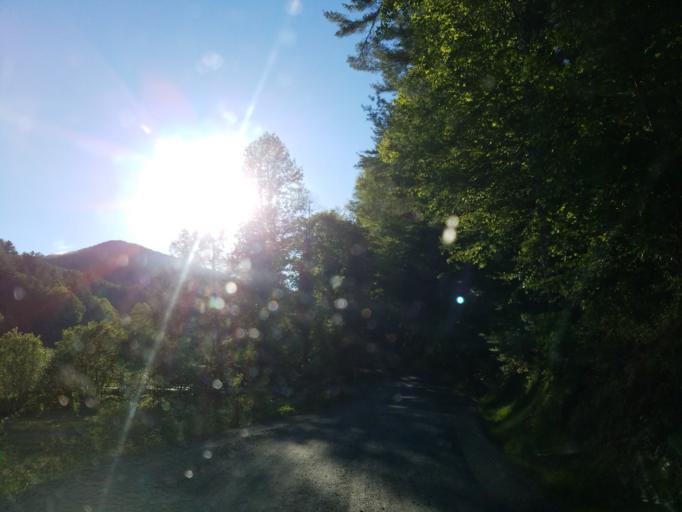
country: US
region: Georgia
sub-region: Fannin County
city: Blue Ridge
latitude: 34.7582
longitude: -84.2633
